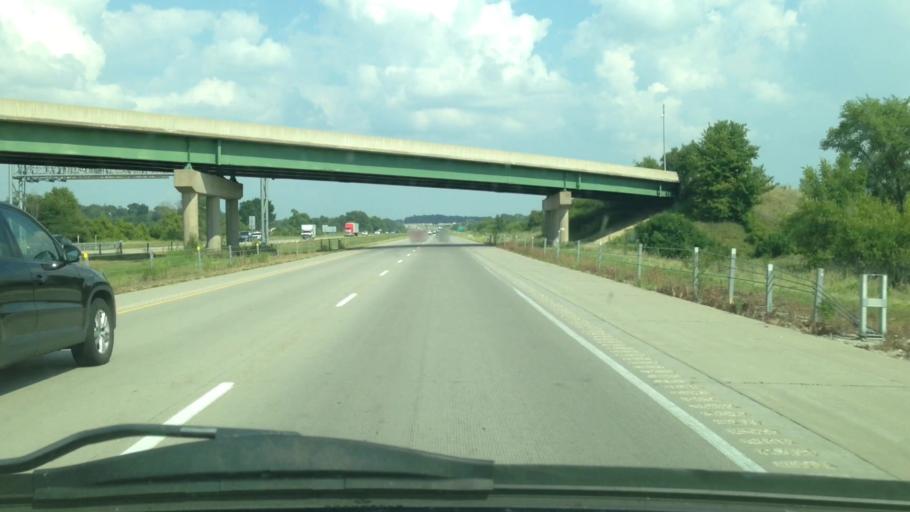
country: US
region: Iowa
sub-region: Black Hawk County
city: Elk Run Heights
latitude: 42.4512
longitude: -92.2382
